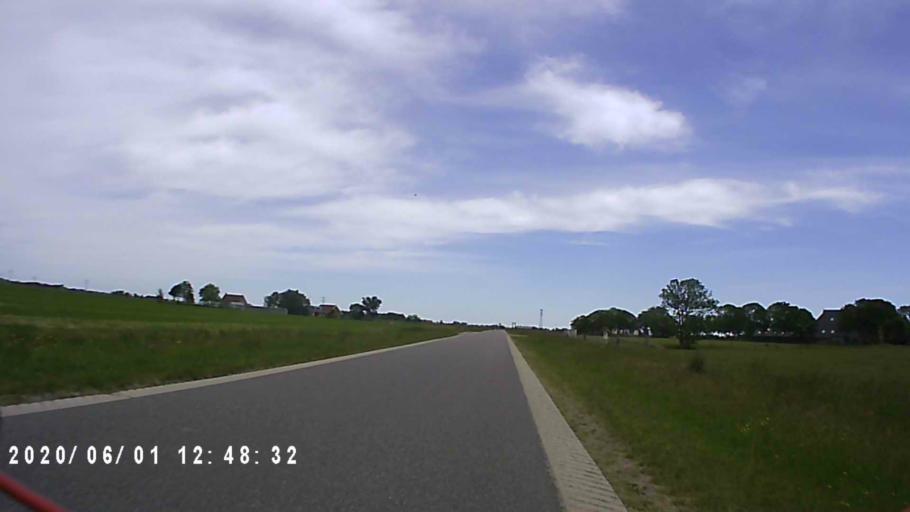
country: NL
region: Friesland
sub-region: Gemeente Franekeradeel
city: Franeker
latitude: 53.1290
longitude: 5.4928
